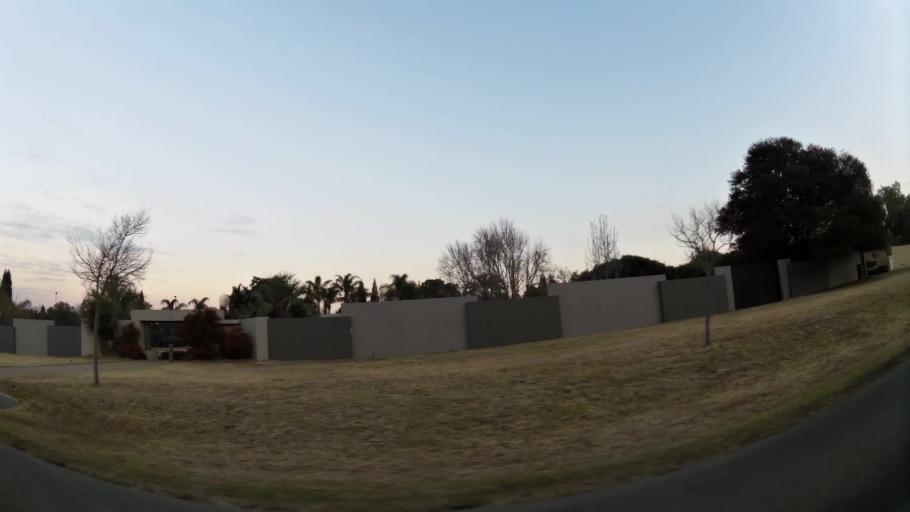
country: ZA
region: Gauteng
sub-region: City of Johannesburg Metropolitan Municipality
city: Midrand
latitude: -25.9819
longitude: 28.0664
